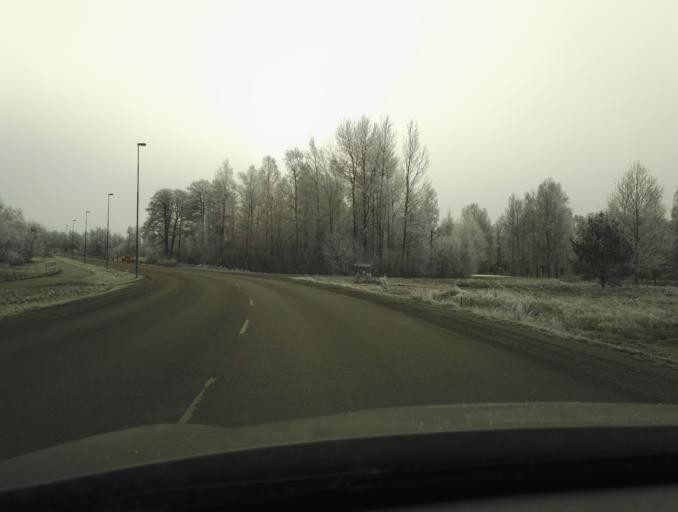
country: SE
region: Kronoberg
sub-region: Vaxjo Kommun
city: Vaexjoe
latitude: 56.8824
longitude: 14.7338
